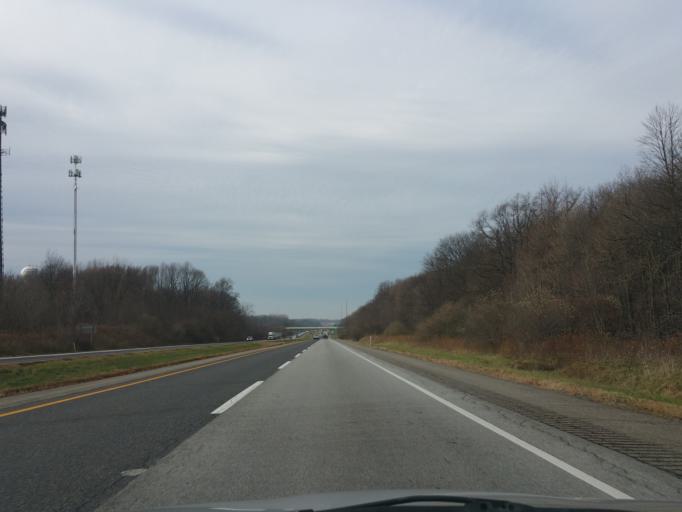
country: US
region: Indiana
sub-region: LaPorte County
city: Westville
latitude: 41.5926
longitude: -86.8866
